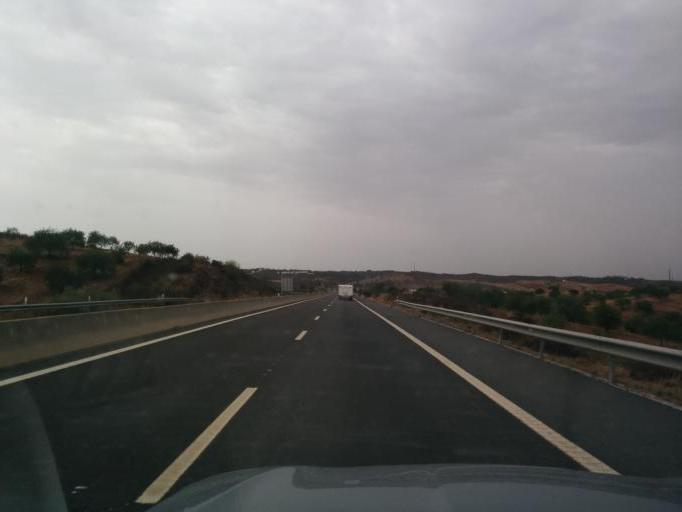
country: PT
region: Faro
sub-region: Castro Marim
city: Castro Marim
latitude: 37.2129
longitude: -7.4846
